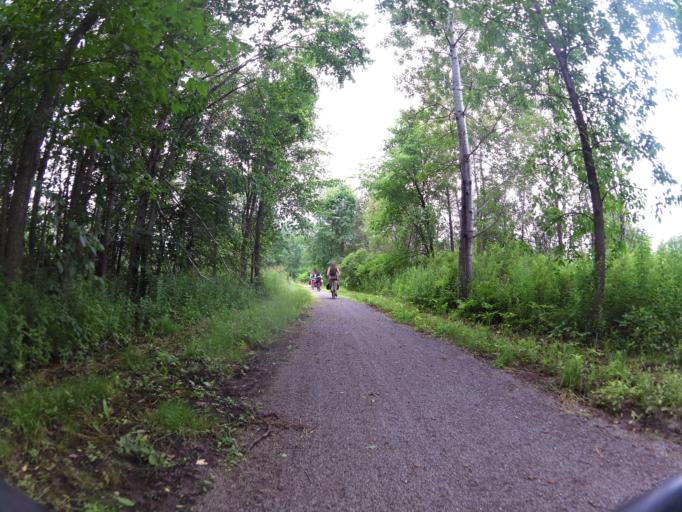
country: CA
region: Ontario
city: Bells Corners
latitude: 45.0226
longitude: -75.6870
